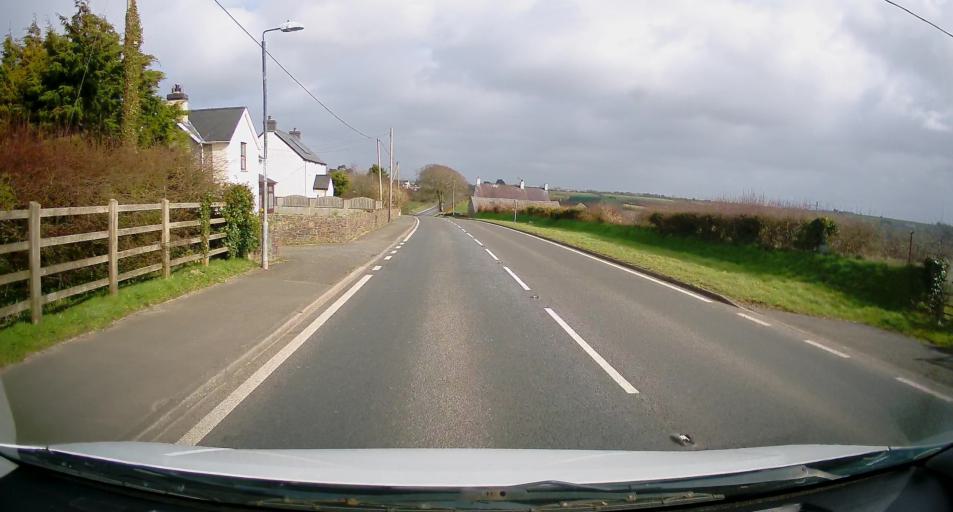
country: GB
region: Wales
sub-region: County of Ceredigion
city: Aberporth
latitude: 52.1120
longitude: -4.5570
